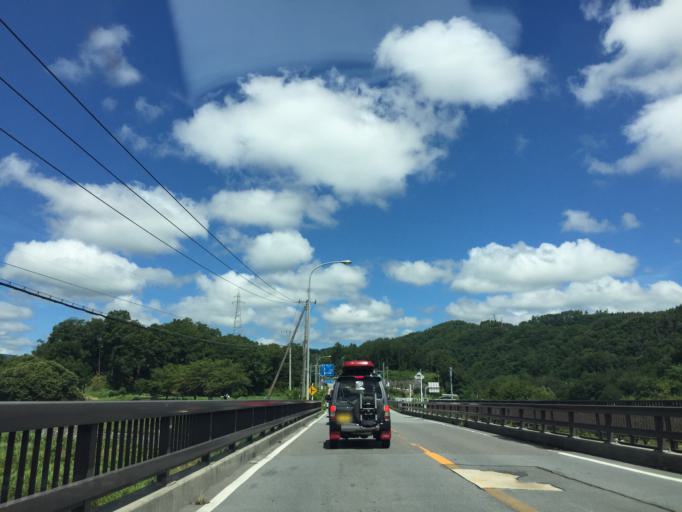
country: JP
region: Yamanashi
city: Nirasaki
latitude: 35.8004
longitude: 138.3564
